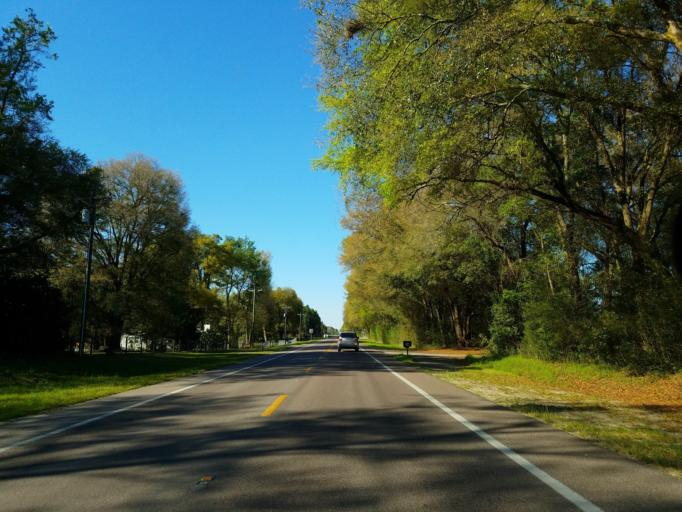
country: US
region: Florida
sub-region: Gilchrist County
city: Trenton
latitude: 29.6882
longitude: -82.8573
